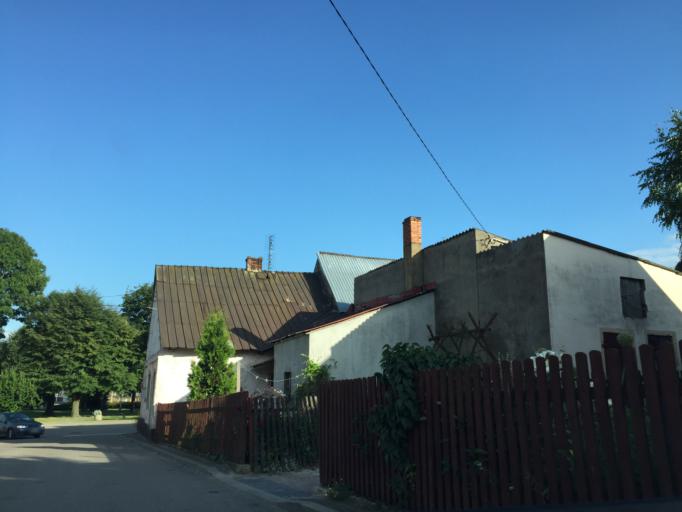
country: PL
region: Podlasie
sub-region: Powiat grajewski
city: Rajgrod
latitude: 53.7301
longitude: 22.6890
